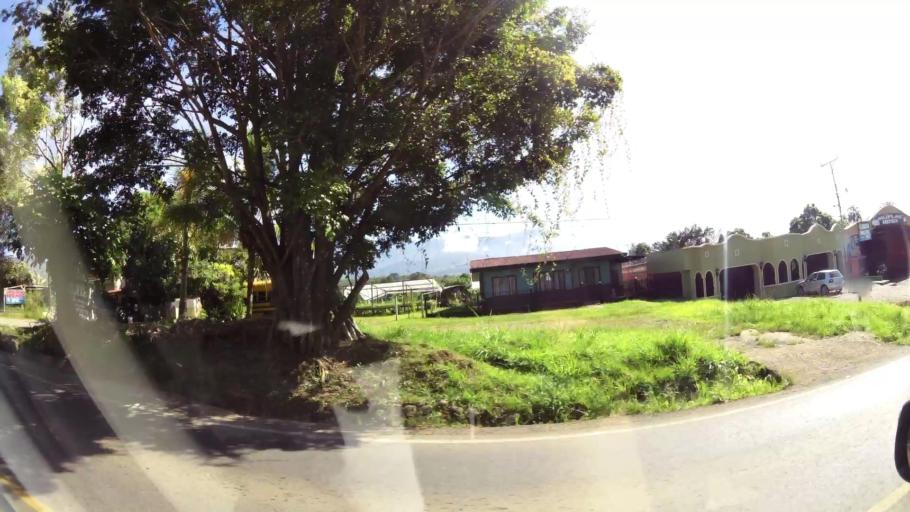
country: CR
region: San Jose
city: San Isidro
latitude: 9.3842
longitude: -83.7067
